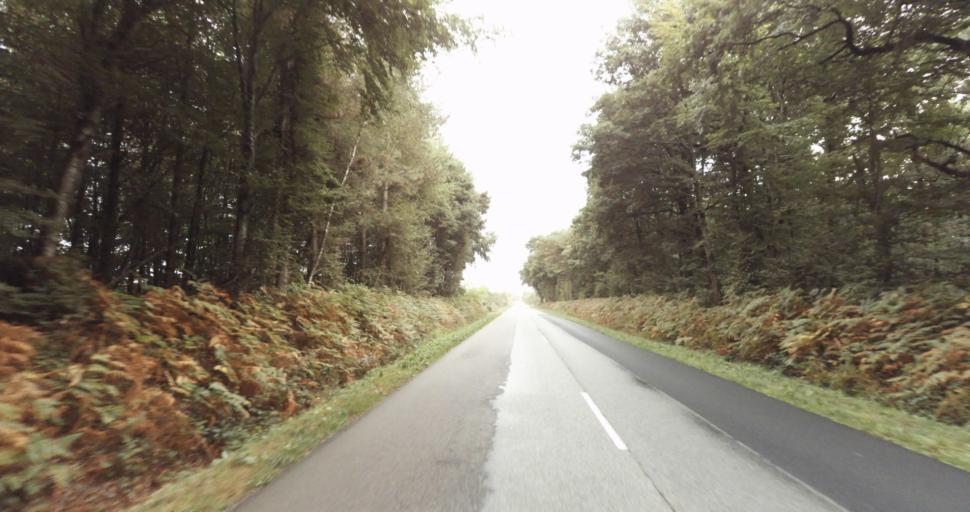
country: FR
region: Lower Normandy
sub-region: Departement de l'Orne
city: Trun
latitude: 48.8881
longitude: 0.1019
